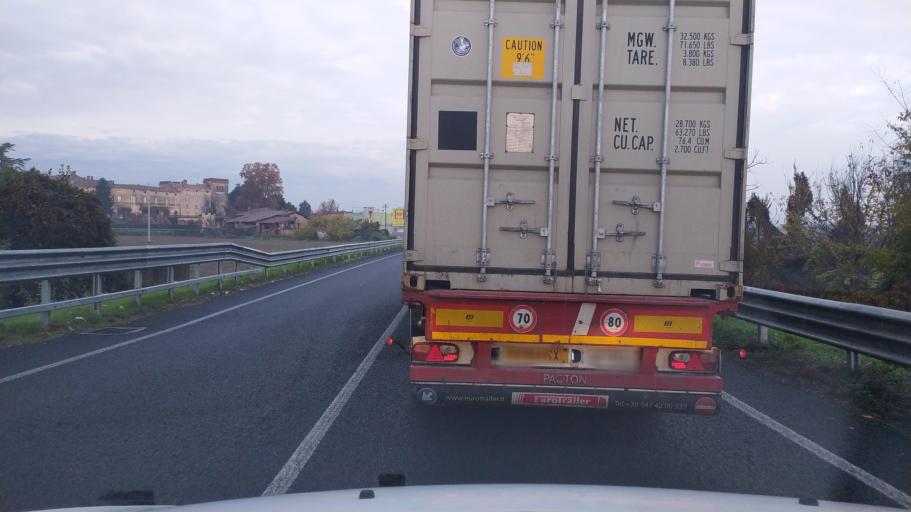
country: IT
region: Lombardy
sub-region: Provincia di Bergamo
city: Calcio
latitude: 45.5053
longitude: 9.8590
